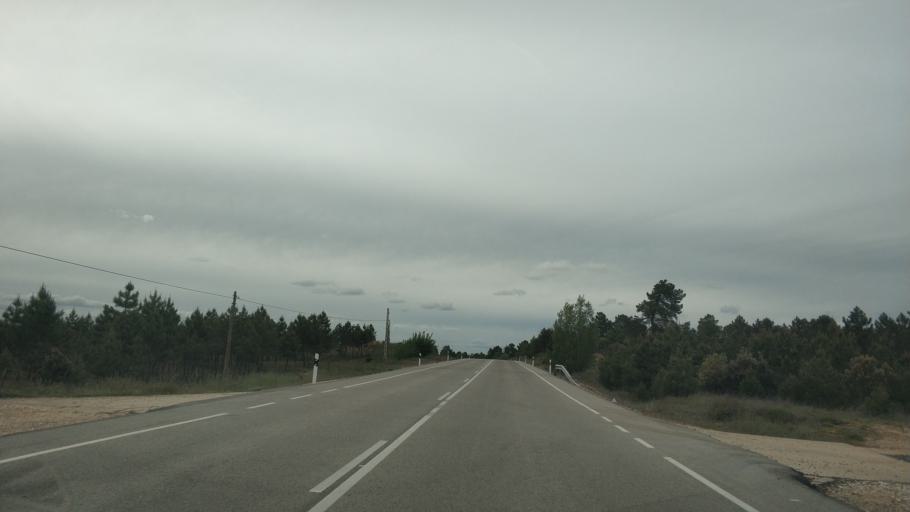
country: ES
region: Castille and Leon
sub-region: Provincia de Soria
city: Quintanas de Gormaz
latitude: 41.5271
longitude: -2.9436
